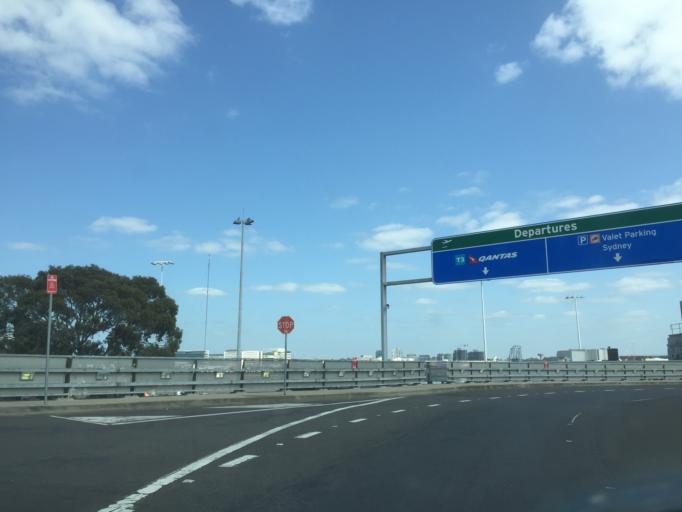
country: AU
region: New South Wales
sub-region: Botany Bay
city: Mascot
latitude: -33.9336
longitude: 151.1786
